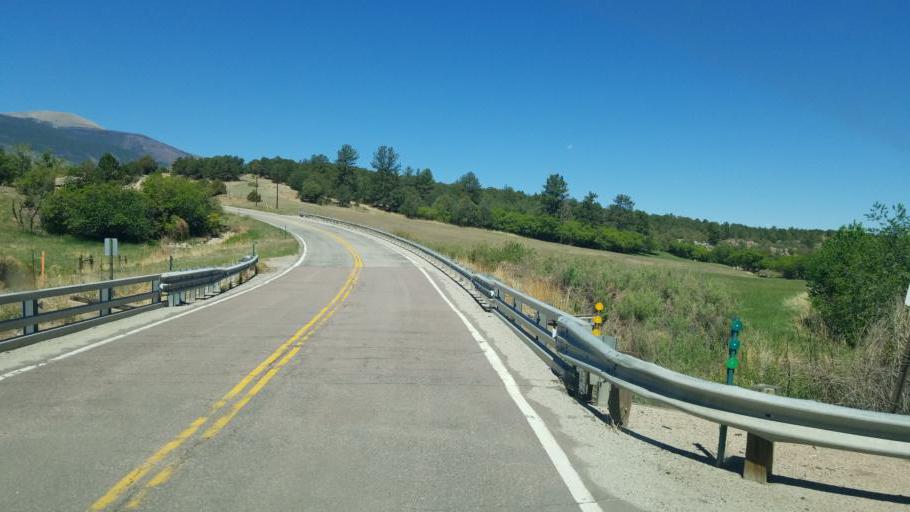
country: US
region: Colorado
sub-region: Custer County
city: Westcliffe
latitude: 38.2635
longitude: -105.6014
